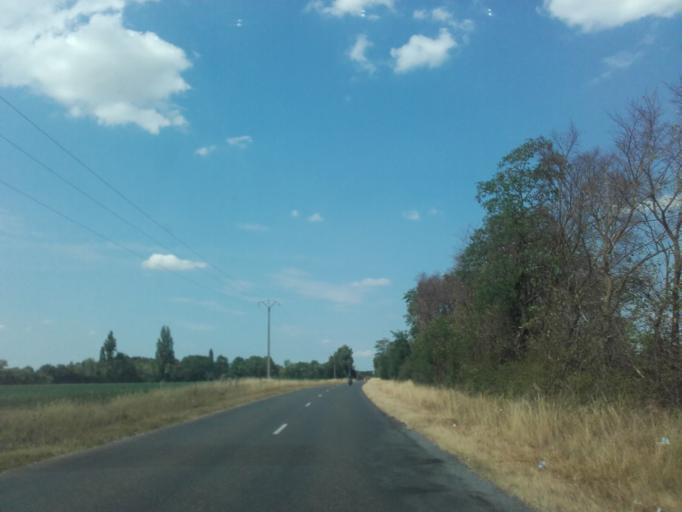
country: FR
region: Rhone-Alpes
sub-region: Departement de l'Ain
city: Loyettes
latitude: 45.7882
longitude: 5.2096
